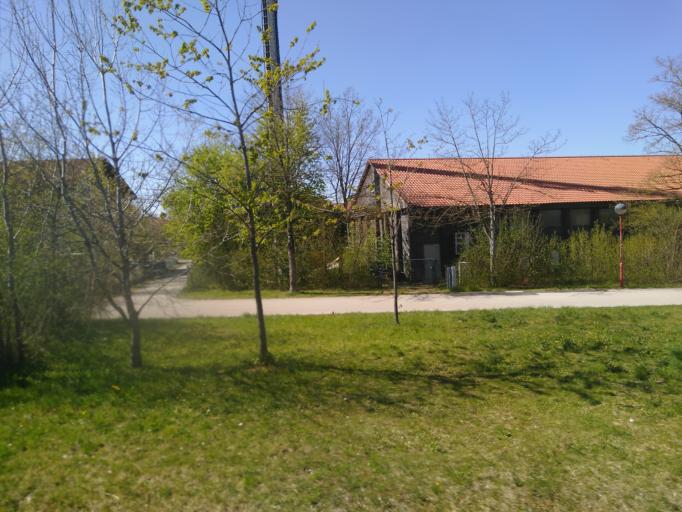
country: DE
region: Bavaria
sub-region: Upper Bavaria
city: Oberhaching
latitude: 48.0339
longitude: 11.5913
